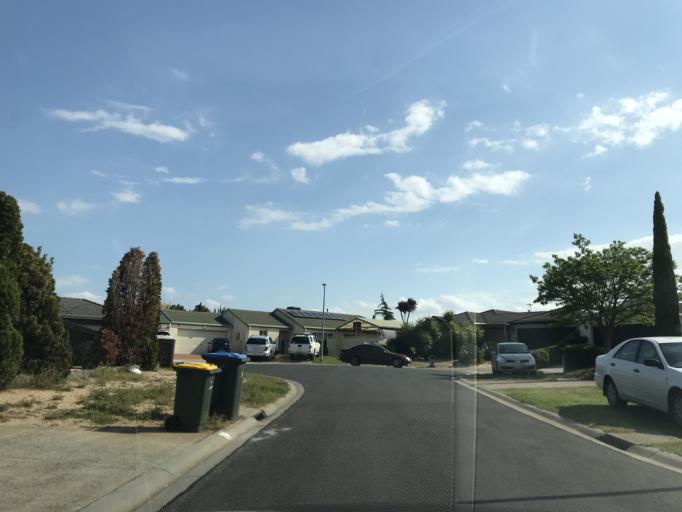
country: AU
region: Victoria
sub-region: Wyndham
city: Hoppers Crossing
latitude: -37.8677
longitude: 144.7119
